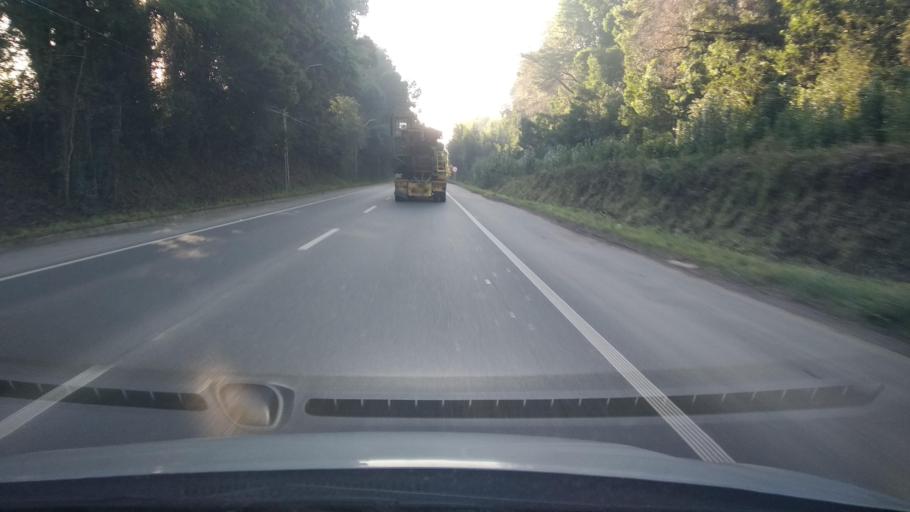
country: CL
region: Los Lagos
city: Las Animas
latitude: -39.7785
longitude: -73.2165
